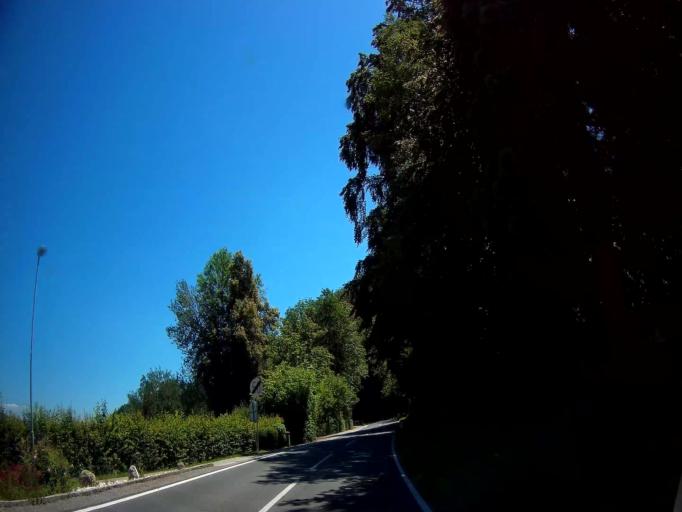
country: AT
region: Carinthia
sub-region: Politischer Bezirk Klagenfurt Land
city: Keutschach am See
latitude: 46.6101
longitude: 14.2116
